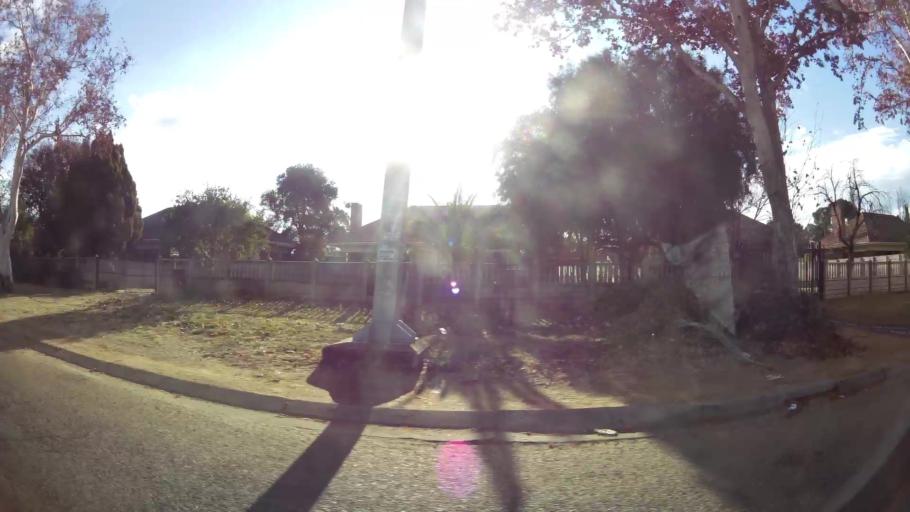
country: ZA
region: Orange Free State
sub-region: Lejweleputswa District Municipality
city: Welkom
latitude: -27.9882
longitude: 26.7543
